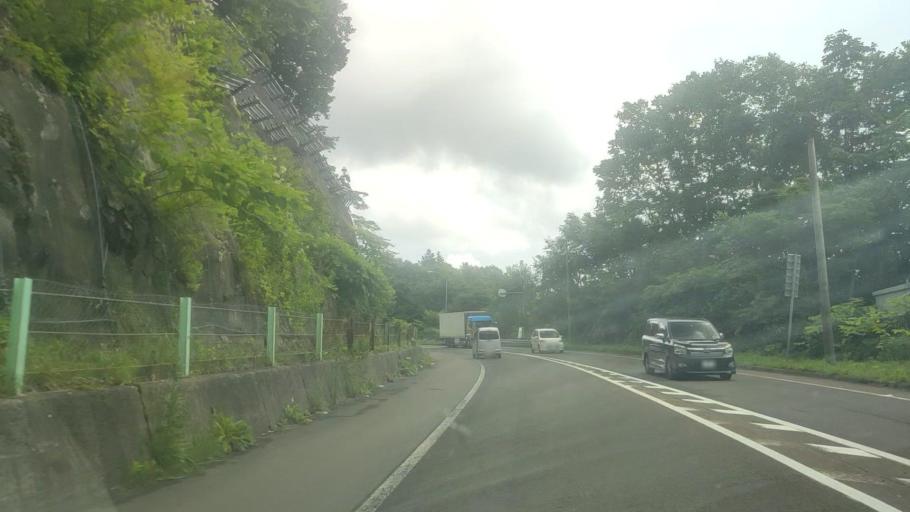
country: JP
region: Hokkaido
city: Niseko Town
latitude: 42.5979
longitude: 140.4622
